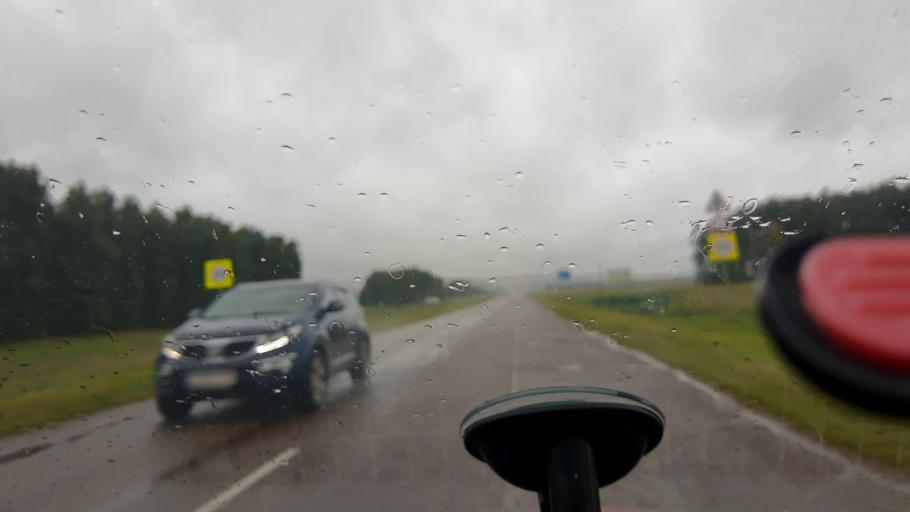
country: RU
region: Bashkortostan
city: Chekmagush
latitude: 55.1167
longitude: 54.6619
